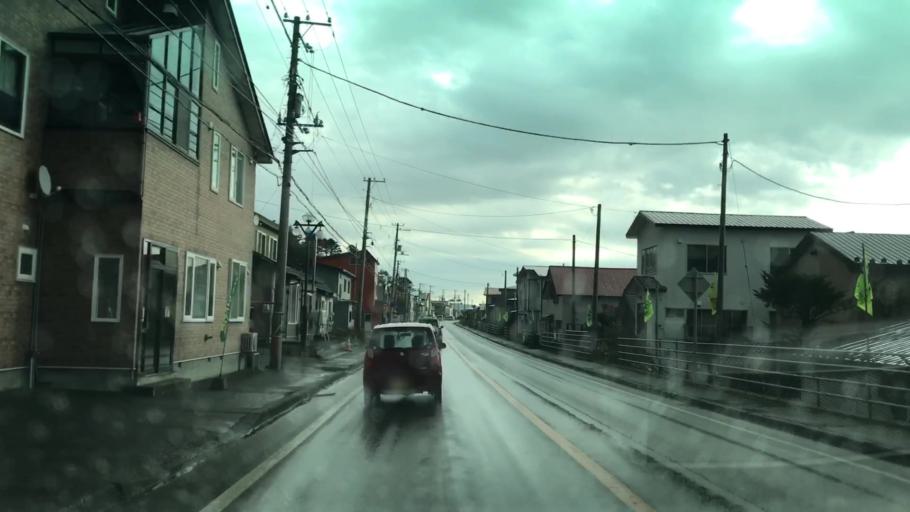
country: JP
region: Hokkaido
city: Shizunai-furukawacho
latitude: 42.1783
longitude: 142.7329
